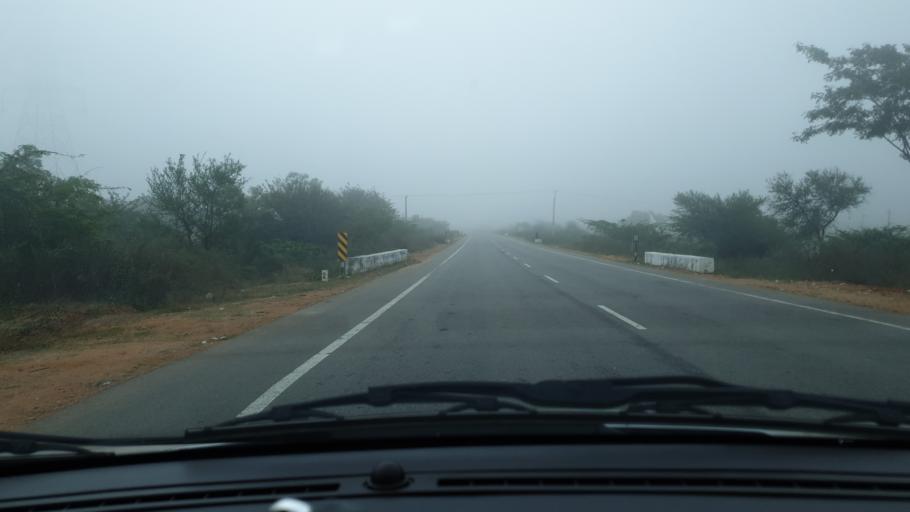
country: IN
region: Telangana
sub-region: Nalgonda
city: Devarkonda
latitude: 16.6056
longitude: 78.6786
